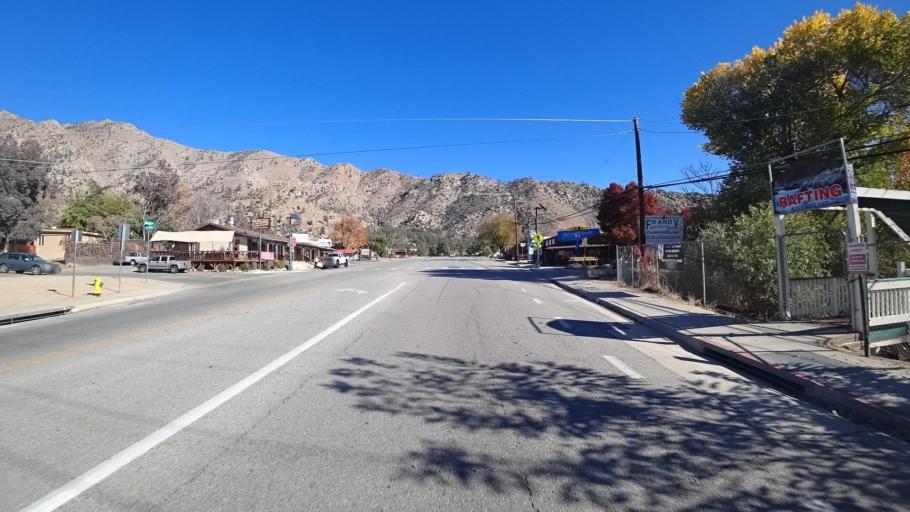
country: US
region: California
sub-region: Kern County
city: Kernville
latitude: 35.7553
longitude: -118.4216
